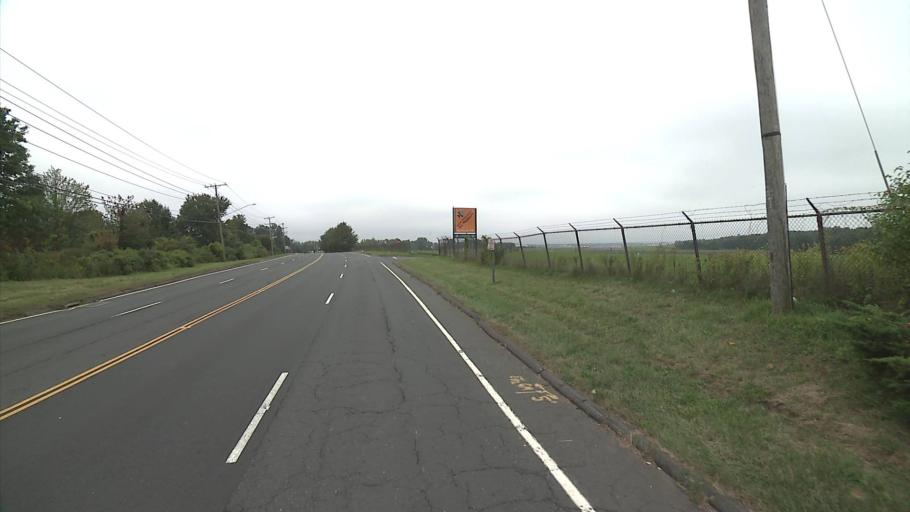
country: US
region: Connecticut
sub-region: Hartford County
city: Suffield Depot
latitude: 41.9567
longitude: -72.6645
